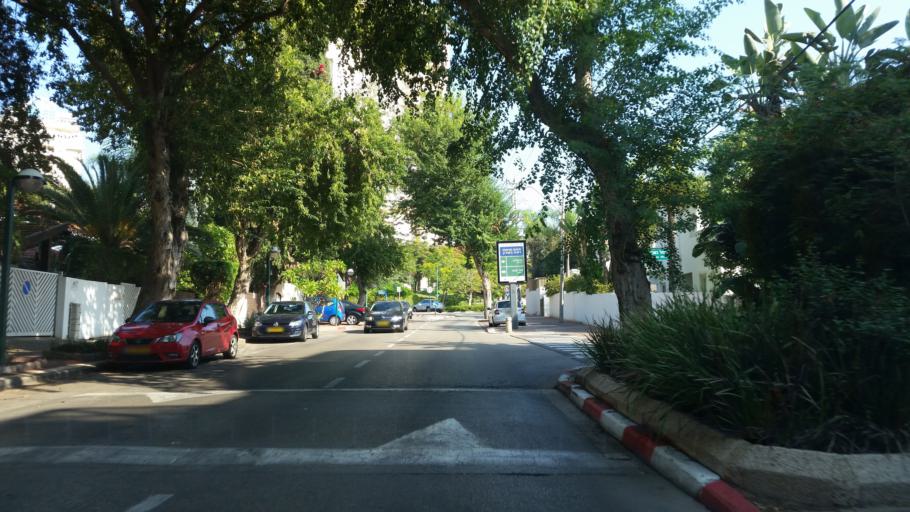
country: IL
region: Tel Aviv
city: Ramat HaSharon
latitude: 32.1491
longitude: 34.8463
